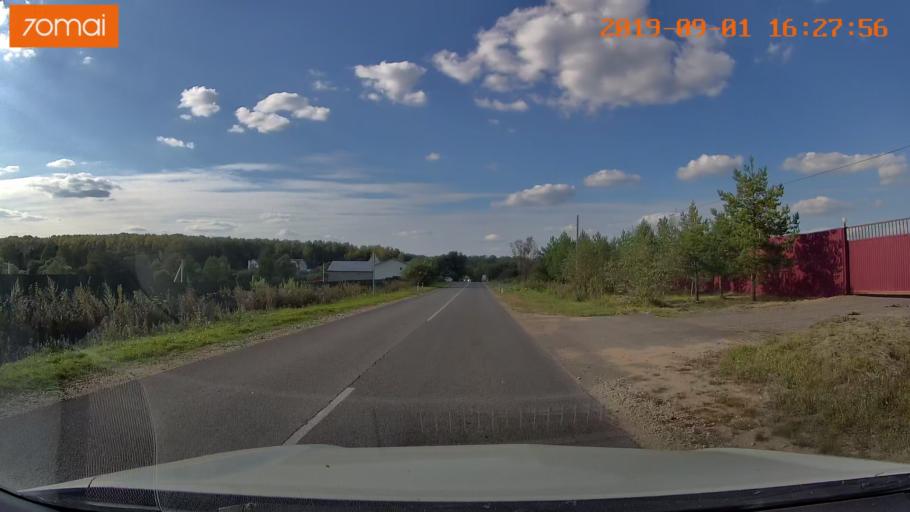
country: RU
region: Kaluga
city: Maloyaroslavets
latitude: 54.9215
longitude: 36.4783
